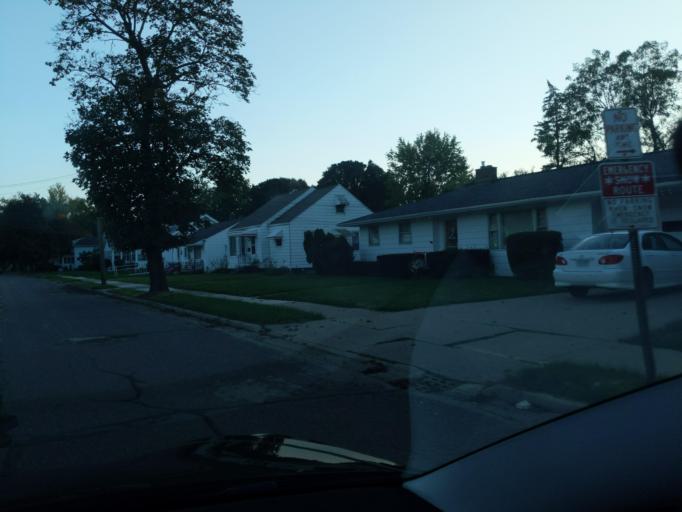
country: US
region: Michigan
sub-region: Jackson County
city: Jackson
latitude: 42.2614
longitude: -84.3844
